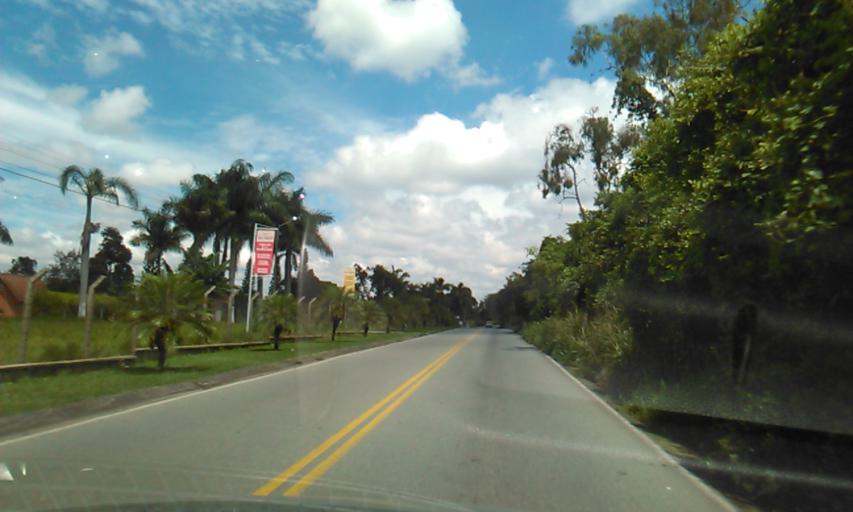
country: CO
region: Quindio
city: Armenia
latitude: 4.4731
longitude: -75.7030
